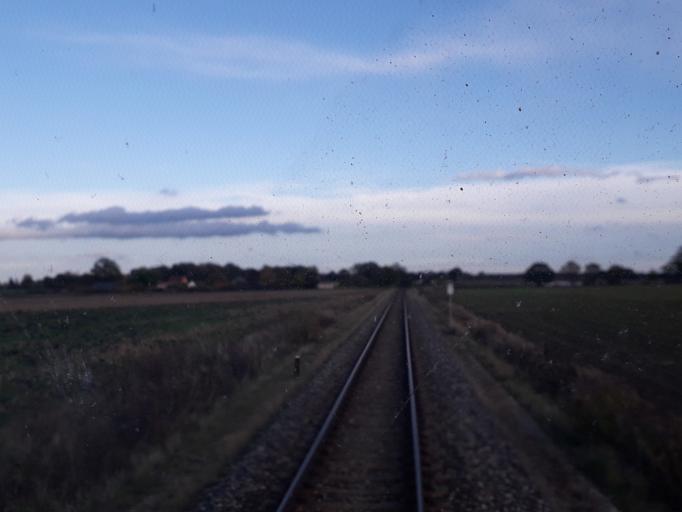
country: DE
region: Brandenburg
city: Pritzwalk
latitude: 53.1485
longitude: 12.2462
